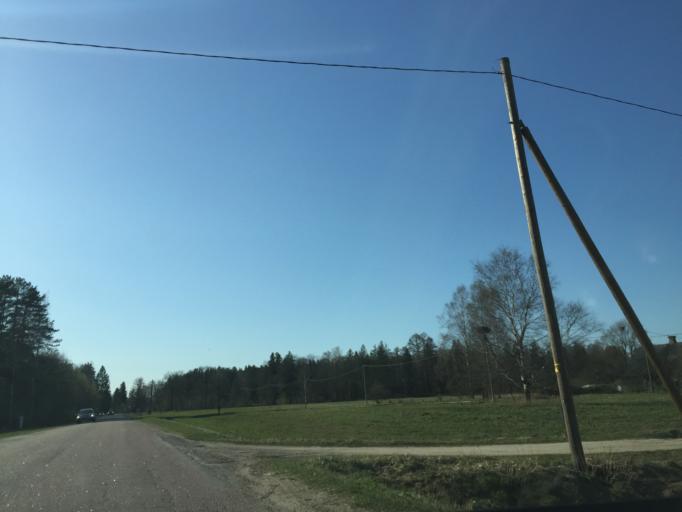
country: LV
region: Ropazu
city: Ropazi
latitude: 56.9698
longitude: 24.6526
